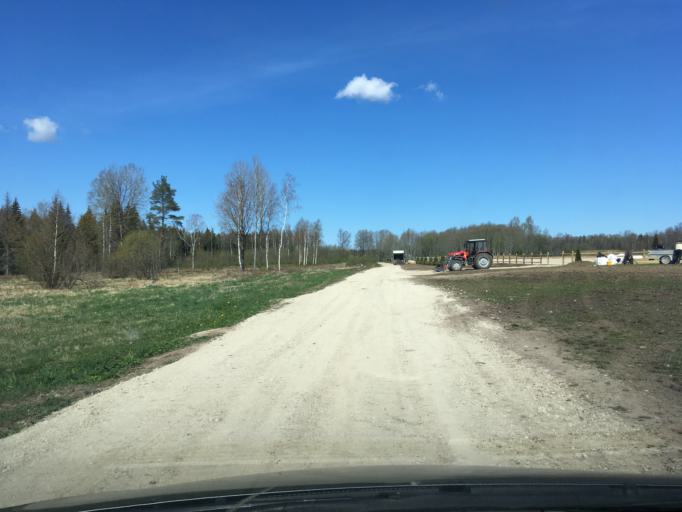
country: EE
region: Harju
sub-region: Raasiku vald
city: Raasiku
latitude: 59.2173
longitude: 25.1568
